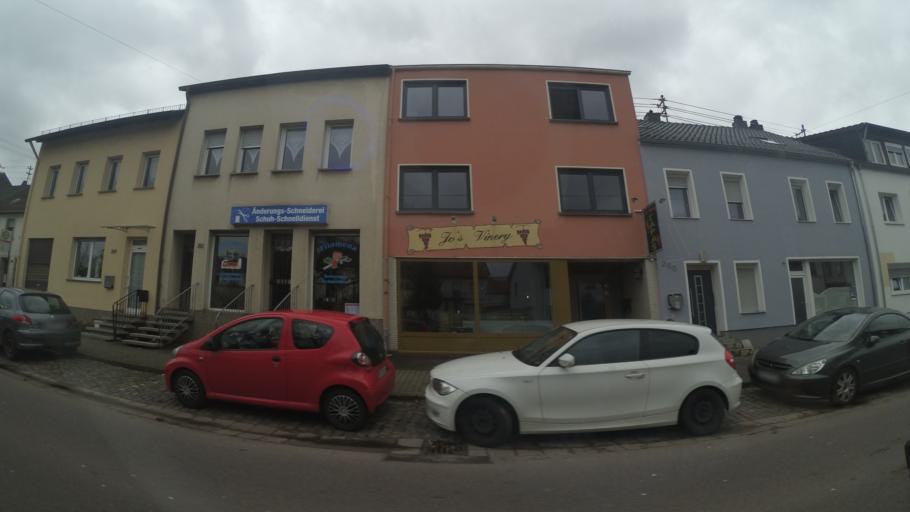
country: DE
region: Saarland
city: Schwalbach
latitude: 49.3054
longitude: 6.8202
